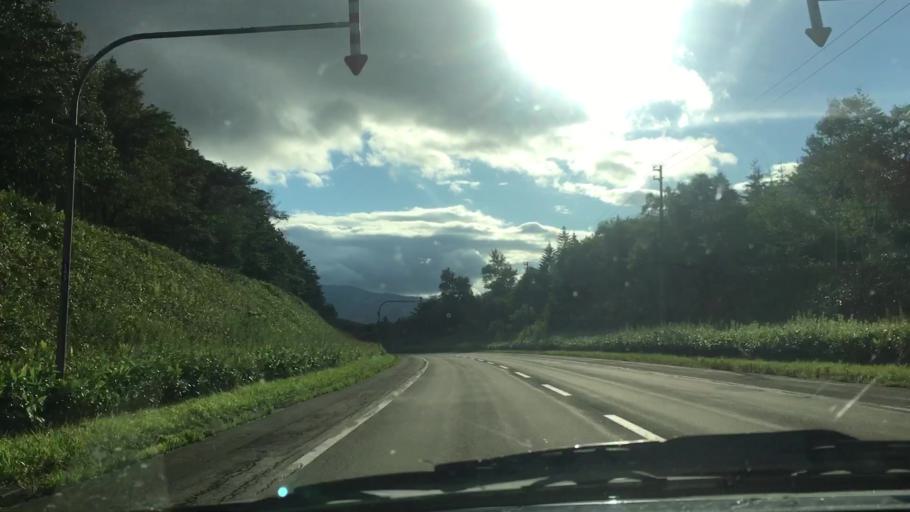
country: JP
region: Hokkaido
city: Shimo-furano
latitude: 43.1352
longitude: 142.7380
